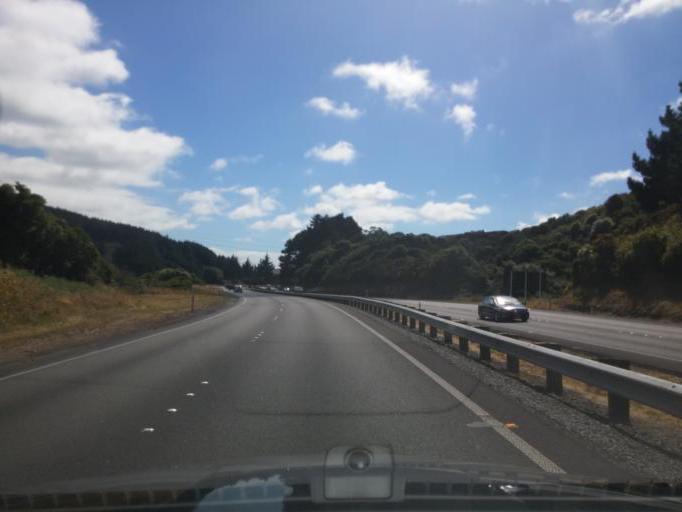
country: NZ
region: Wellington
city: Petone
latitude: -41.2008
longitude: 174.8235
